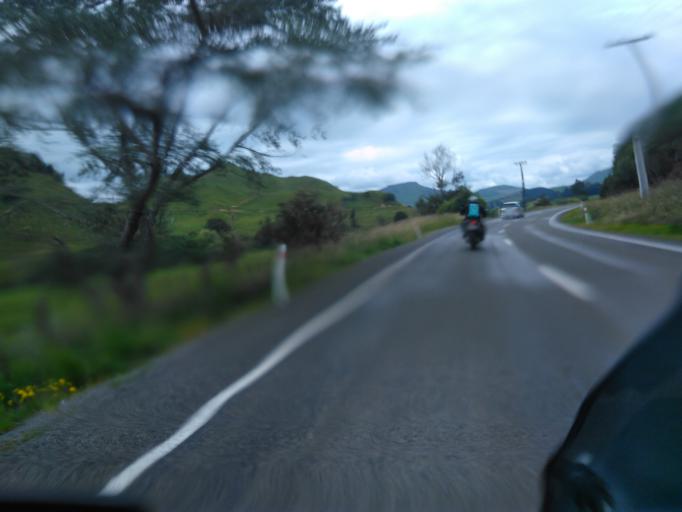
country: NZ
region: Bay of Plenty
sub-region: Opotiki District
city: Opotiki
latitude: -38.3619
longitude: 177.5017
